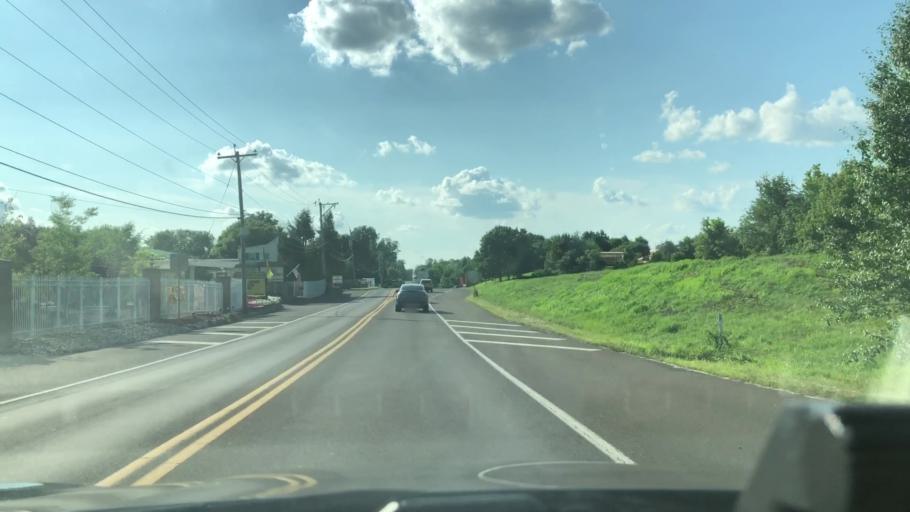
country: US
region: Pennsylvania
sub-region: Montgomery County
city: Montgomeryville
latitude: 40.2773
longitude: -75.2483
